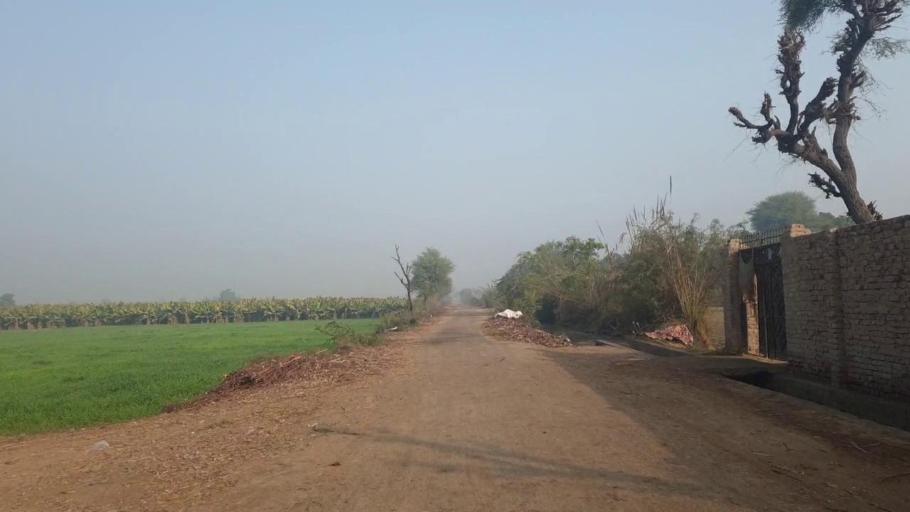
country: PK
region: Sindh
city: Tando Adam
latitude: 25.8135
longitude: 68.6323
